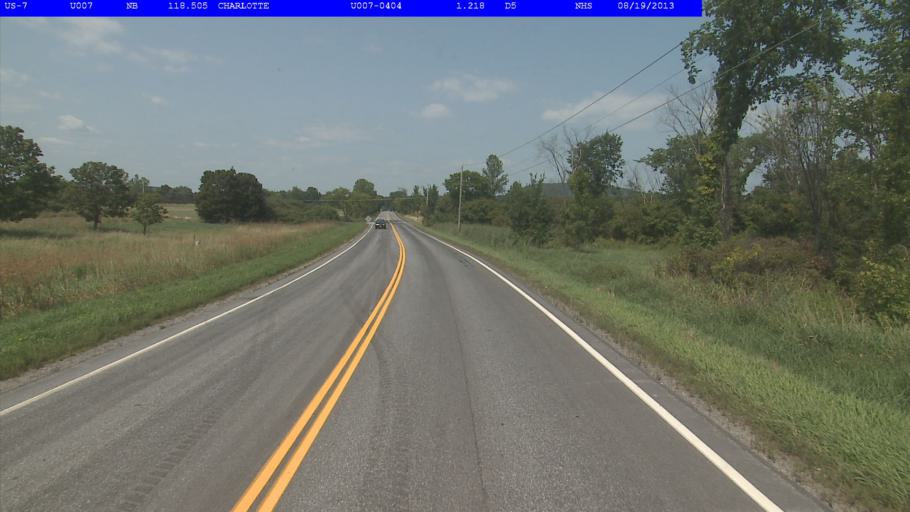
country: US
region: Vermont
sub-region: Addison County
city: Vergennes
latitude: 44.2797
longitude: -73.2355
